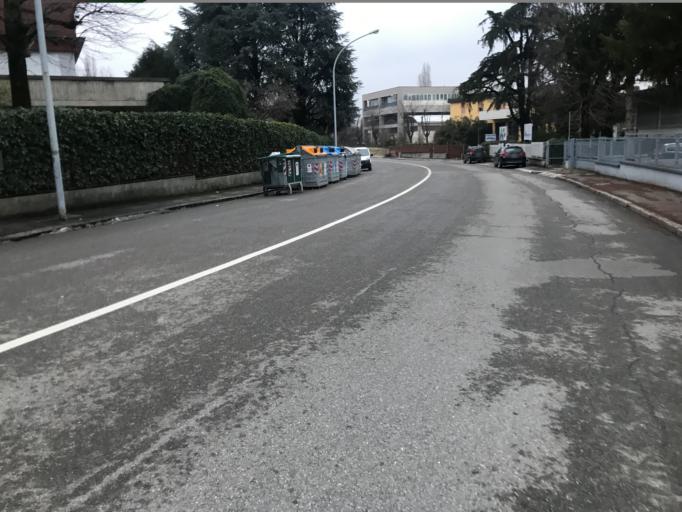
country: IT
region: Emilia-Romagna
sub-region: Provincia di Bologna
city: Trebbo
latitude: 44.5381
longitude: 11.3476
